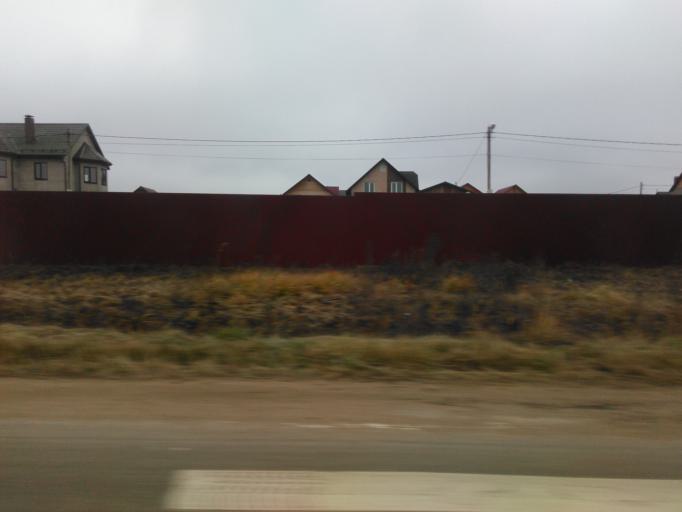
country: RU
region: Moskovskaya
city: Ashukino
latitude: 56.1764
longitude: 37.9345
